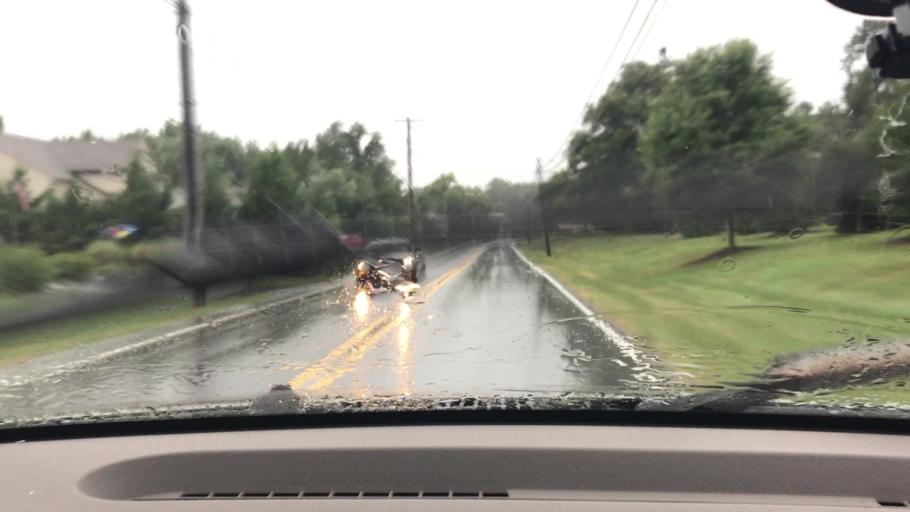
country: US
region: Pennsylvania
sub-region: Lancaster County
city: Elizabethtown
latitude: 40.1379
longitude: -76.6139
